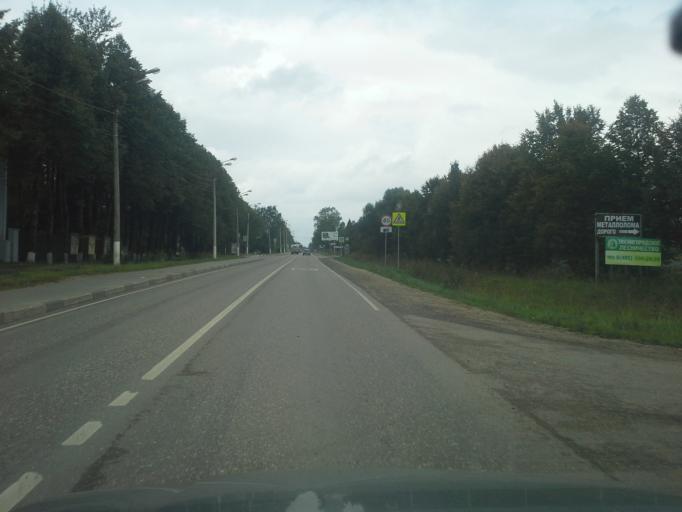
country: RU
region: Moskovskaya
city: Ruza
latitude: 55.7110
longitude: 36.1786
